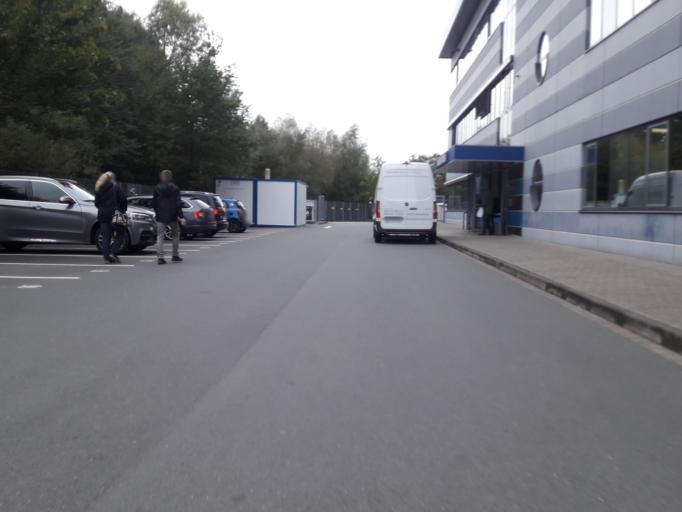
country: DE
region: North Rhine-Westphalia
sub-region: Regierungsbezirk Detmold
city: Paderborn
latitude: 51.7305
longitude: 8.7100
